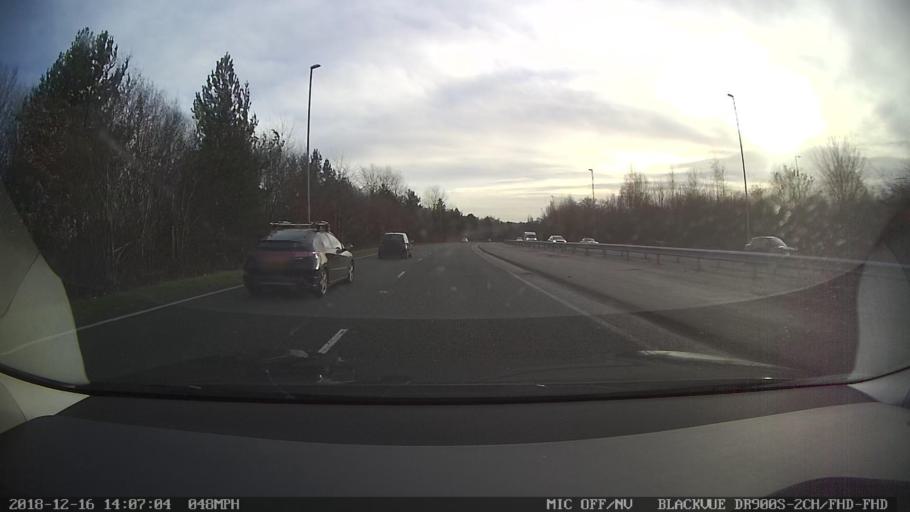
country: GB
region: England
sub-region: Borough of Stockport
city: Cheadle Hulme
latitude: 53.3766
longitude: -2.2128
